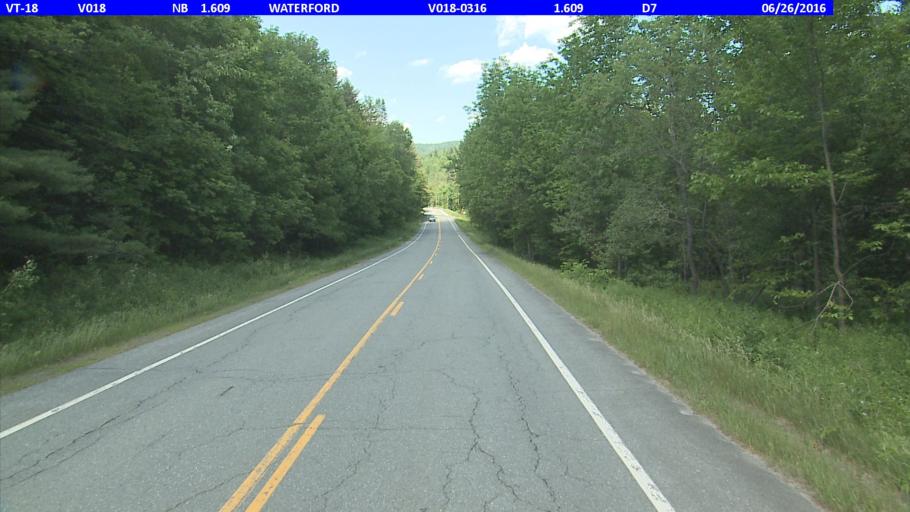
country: US
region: Vermont
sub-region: Caledonia County
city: Saint Johnsbury
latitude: 44.3601
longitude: -71.9057
